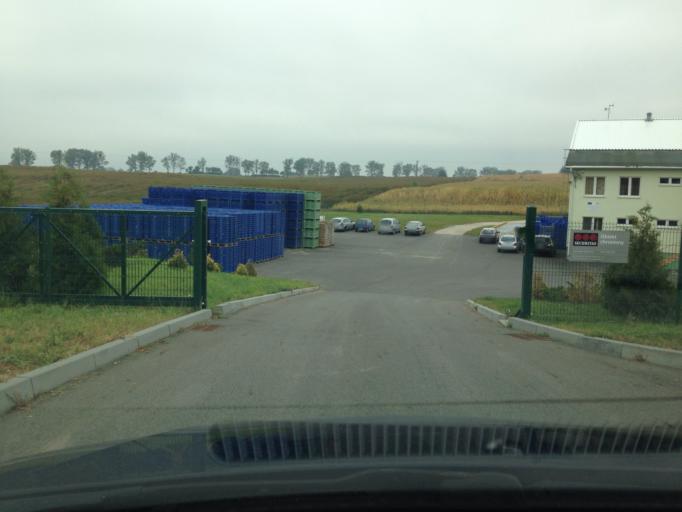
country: PL
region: Kujawsko-Pomorskie
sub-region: Powiat brodnicki
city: Gorzno
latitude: 53.2125
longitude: 19.6350
